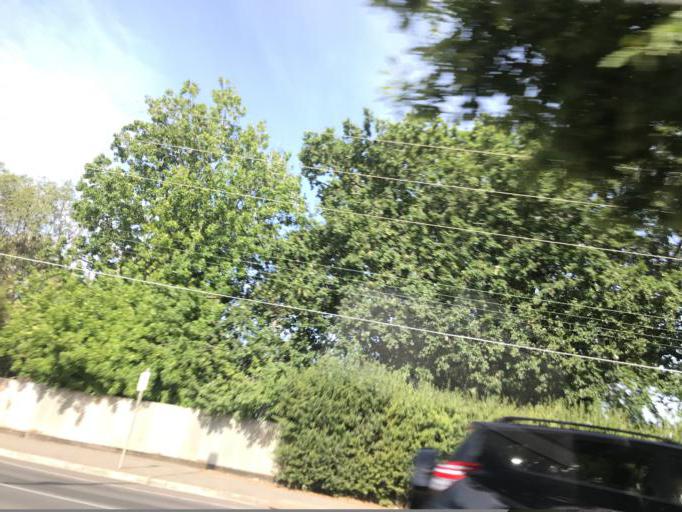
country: AU
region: Victoria
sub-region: Ballarat North
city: Newington
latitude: -37.5543
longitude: 143.8193
